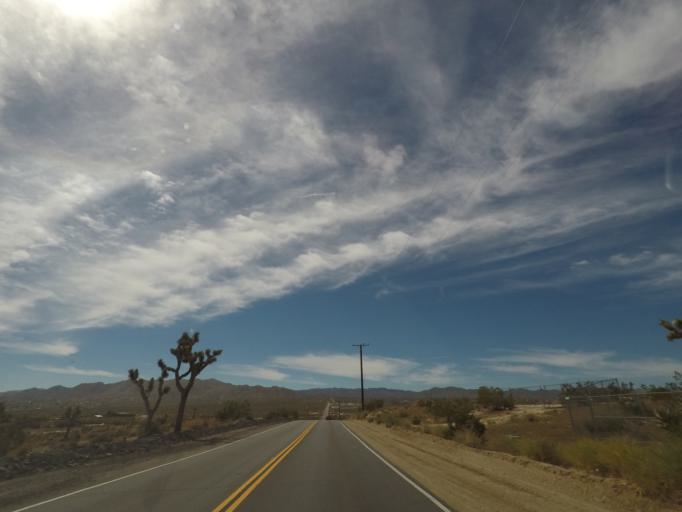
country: US
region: California
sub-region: San Bernardino County
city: Joshua Tree
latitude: 34.1457
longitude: -116.3697
